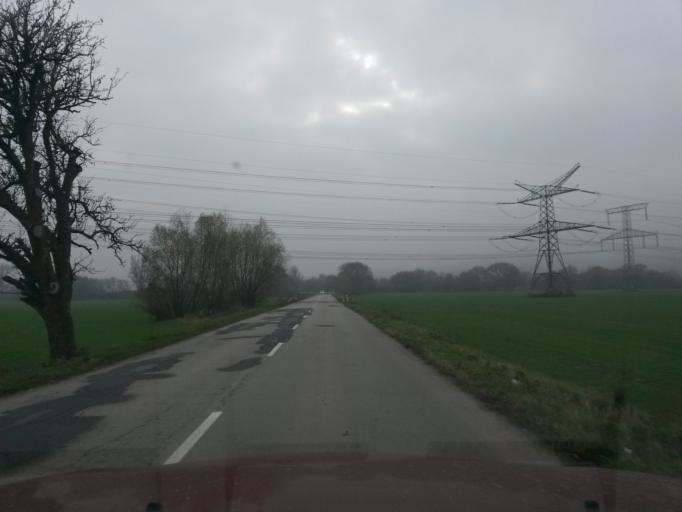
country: SK
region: Presovsky
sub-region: Okres Presov
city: Presov
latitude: 48.8625
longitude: 21.2709
